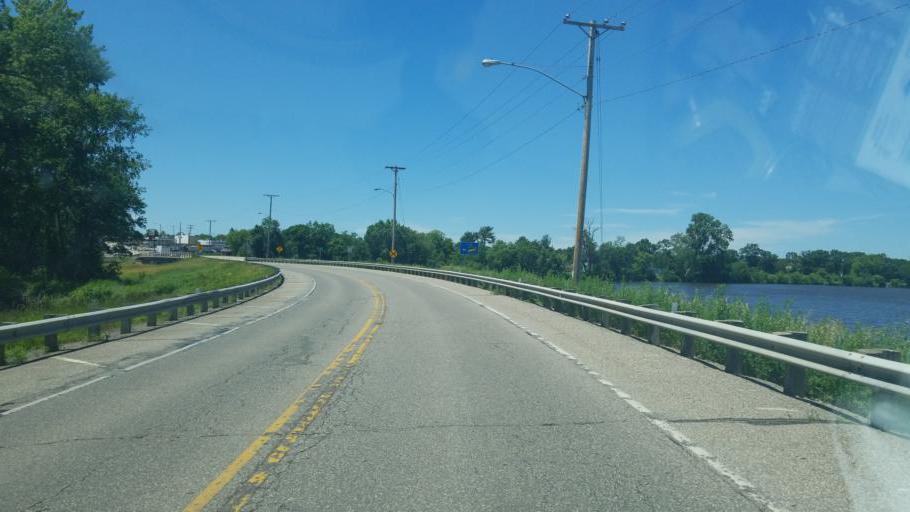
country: US
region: Wisconsin
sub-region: Juneau County
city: New Lisbon
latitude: 44.0279
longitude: -90.0700
